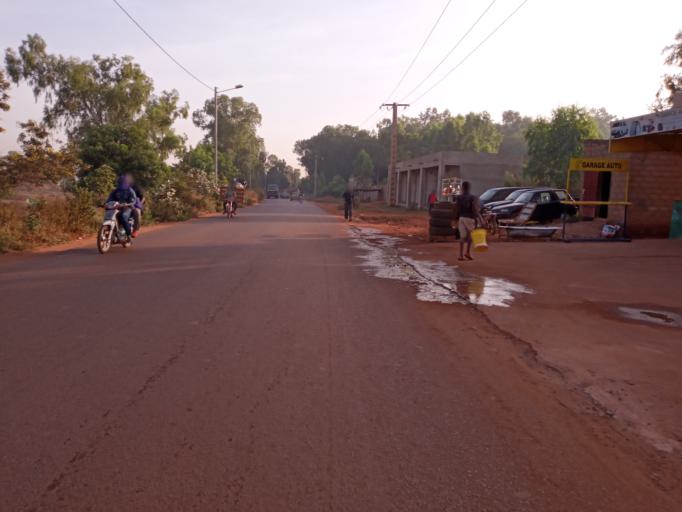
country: ML
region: Bamako
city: Bamako
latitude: 12.6296
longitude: -7.9455
